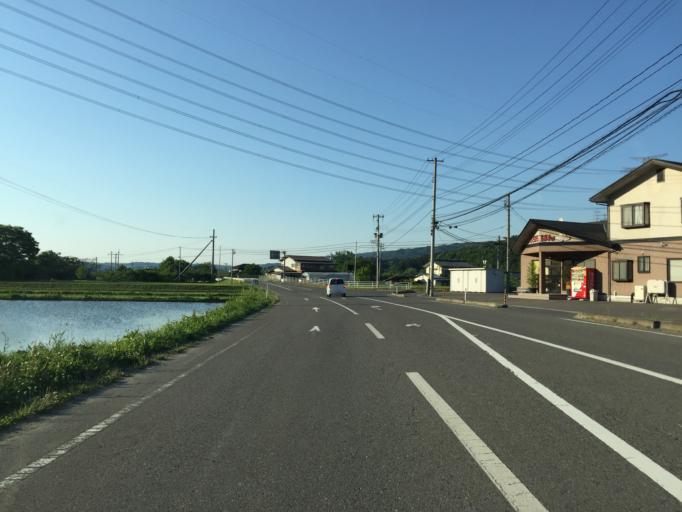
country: JP
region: Ibaraki
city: Daigo
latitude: 36.9449
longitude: 140.4403
